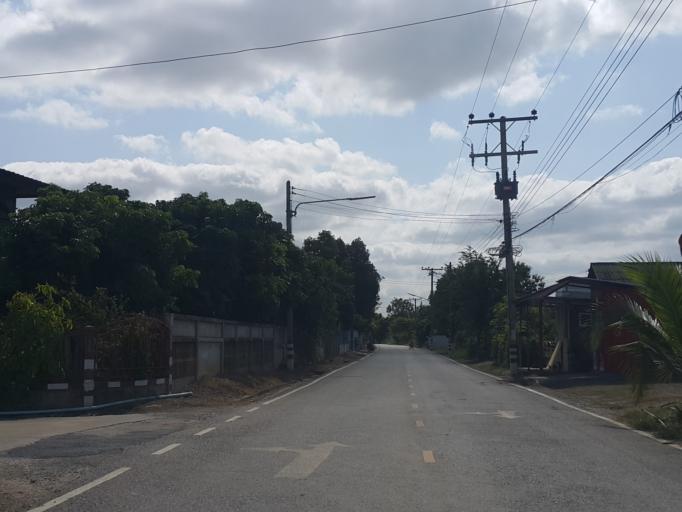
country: TH
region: Lamphun
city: Ban Thi
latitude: 18.5655
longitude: 99.0864
